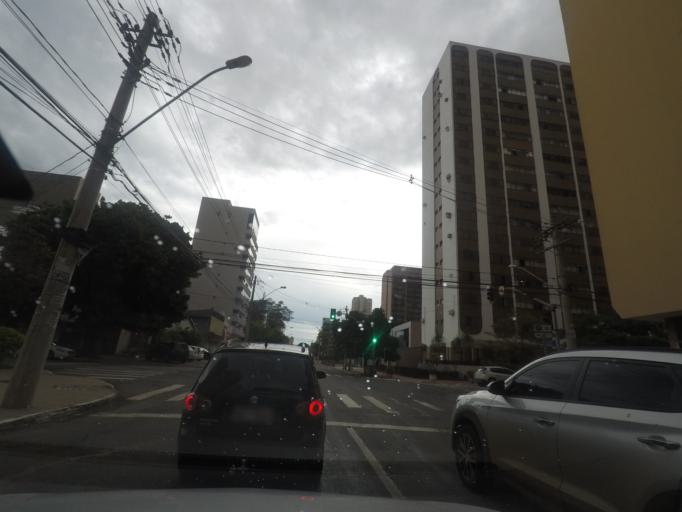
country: BR
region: Goias
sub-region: Goiania
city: Goiania
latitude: -16.6795
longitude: -49.2696
